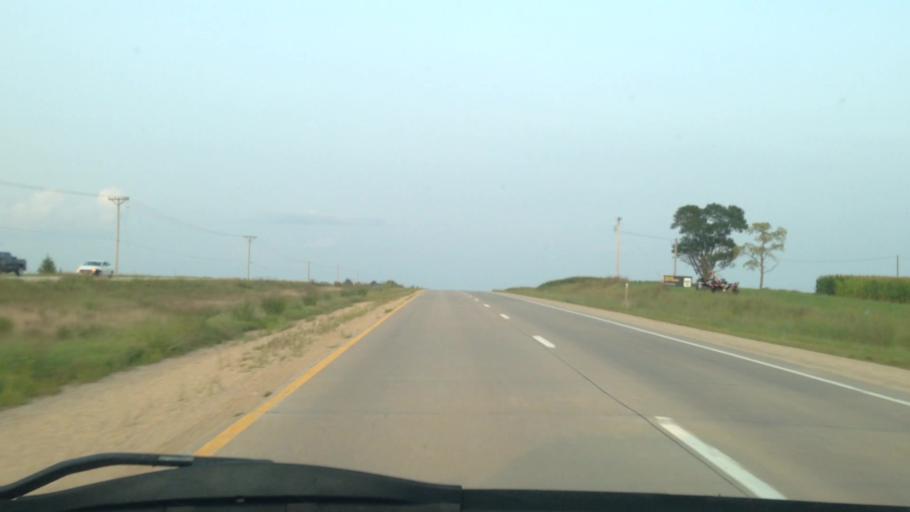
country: US
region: Iowa
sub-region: Benton County
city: Atkins
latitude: 41.9632
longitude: -91.9594
